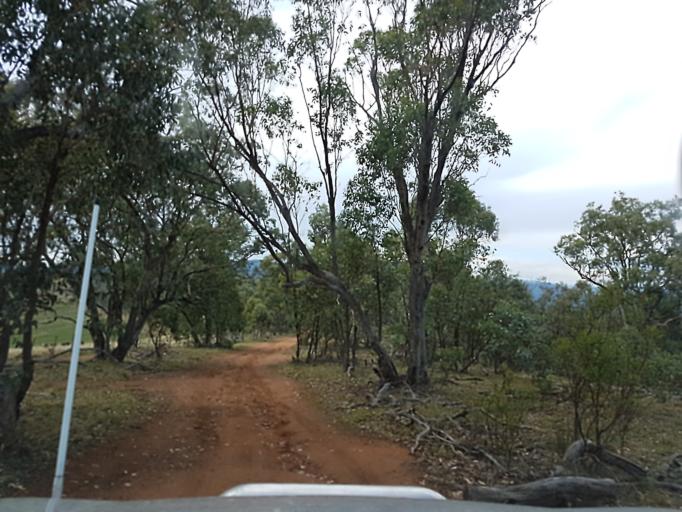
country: AU
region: New South Wales
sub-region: Snowy River
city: Jindabyne
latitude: -36.9661
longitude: 148.3844
